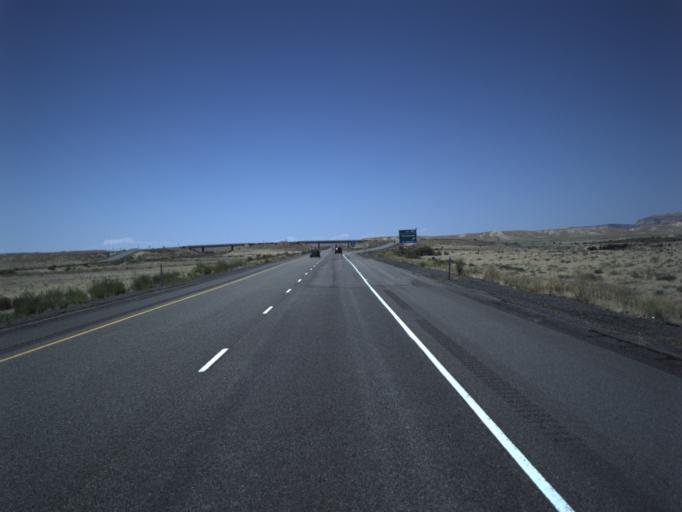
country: US
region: Utah
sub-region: Grand County
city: Moab
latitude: 38.9428
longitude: -109.6053
